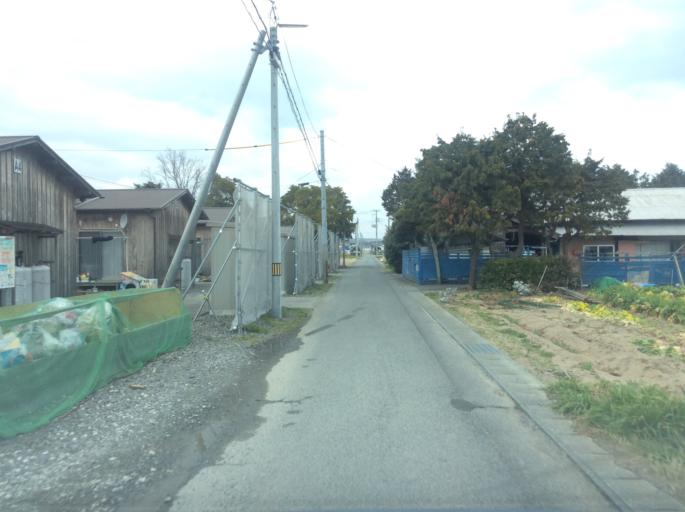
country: JP
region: Fukushima
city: Iwaki
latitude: 37.0778
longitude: 140.9721
